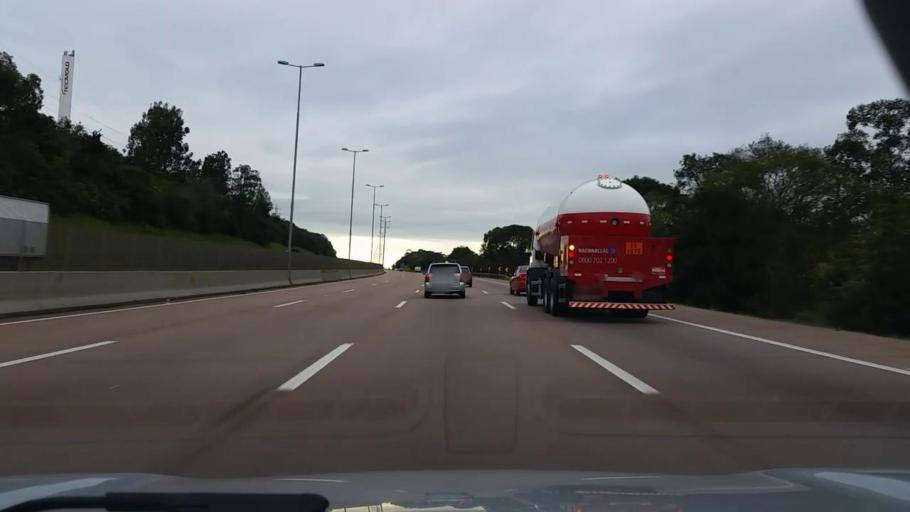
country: BR
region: Rio Grande do Sul
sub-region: Gravatai
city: Gravatai
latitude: -29.9567
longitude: -51.0142
